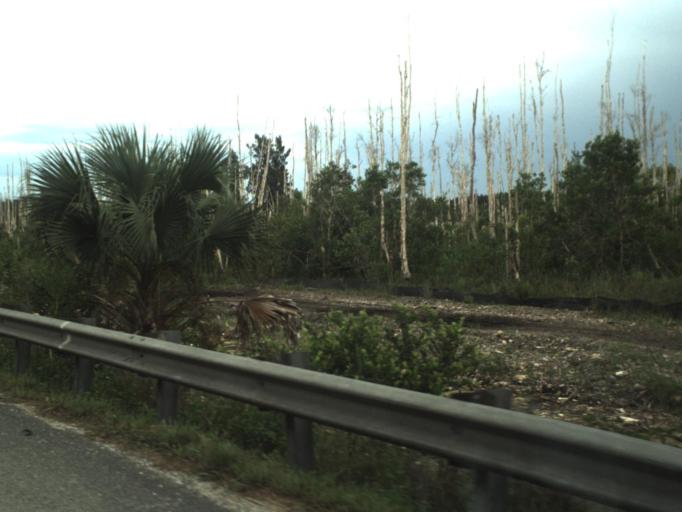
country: US
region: Florida
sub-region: Miami-Dade County
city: Kendall West
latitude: 25.7290
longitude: -80.4801
